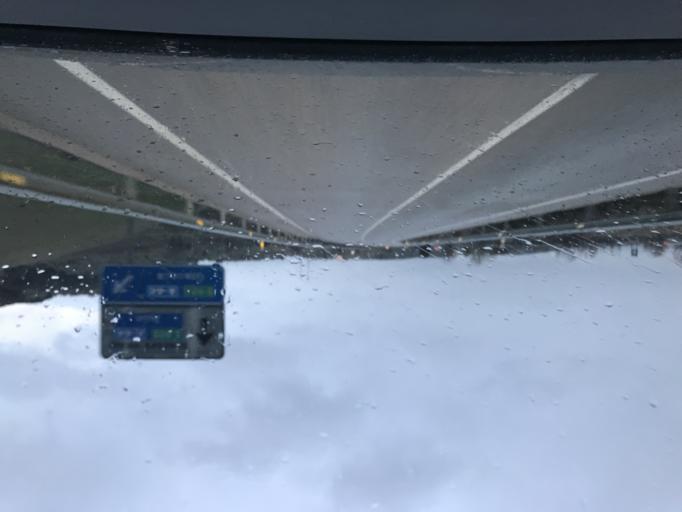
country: ES
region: Andalusia
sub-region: Provincia de Granada
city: Campotejar
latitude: 37.4694
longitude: -3.5746
